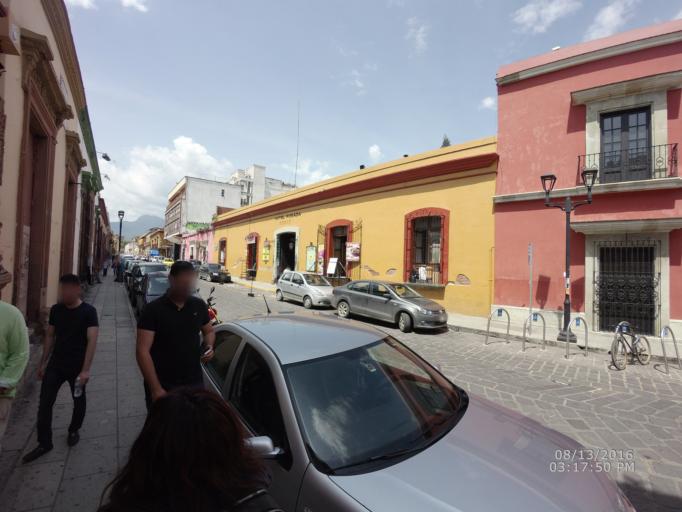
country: MX
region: Oaxaca
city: Oaxaca de Juarez
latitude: 17.0620
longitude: -96.7237
